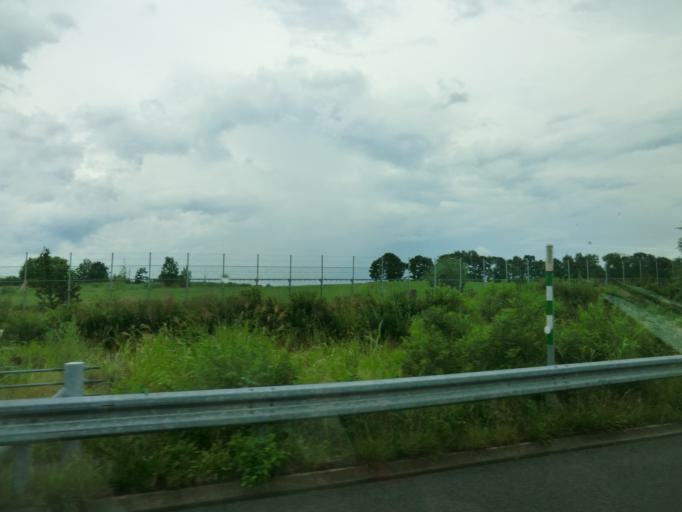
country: JP
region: Hokkaido
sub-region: Asahikawa-shi
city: Asahikawa
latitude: 43.8372
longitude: 142.3770
